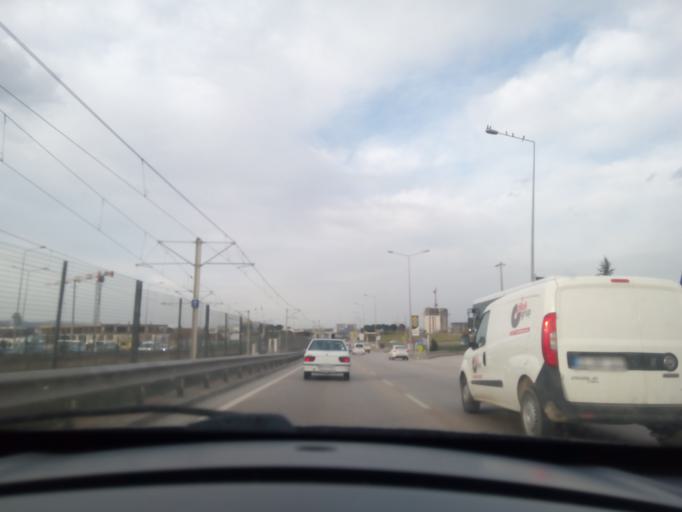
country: TR
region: Bursa
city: Cali
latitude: 40.2122
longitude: 28.9436
